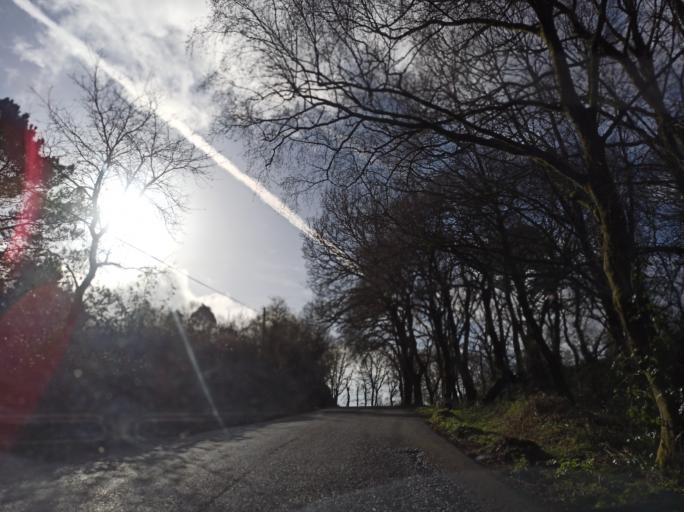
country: ES
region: Galicia
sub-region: Provincia da Coruna
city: Sobrado
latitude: 43.0905
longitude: -7.9696
